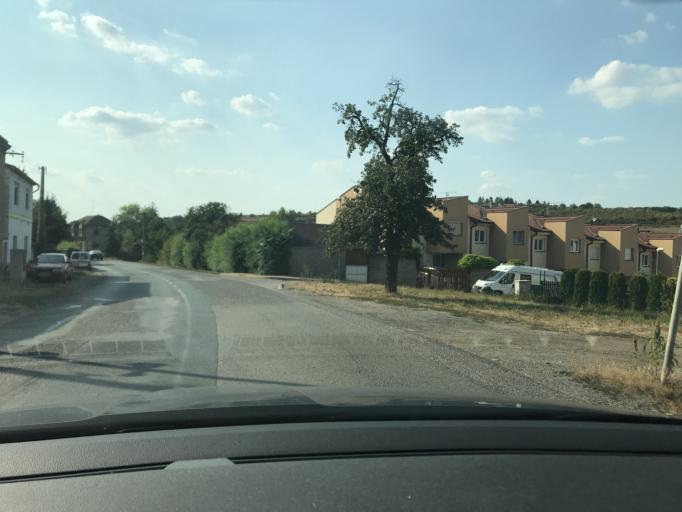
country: CZ
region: Central Bohemia
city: Kralupy nad Vltavou
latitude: 50.2313
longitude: 14.2894
